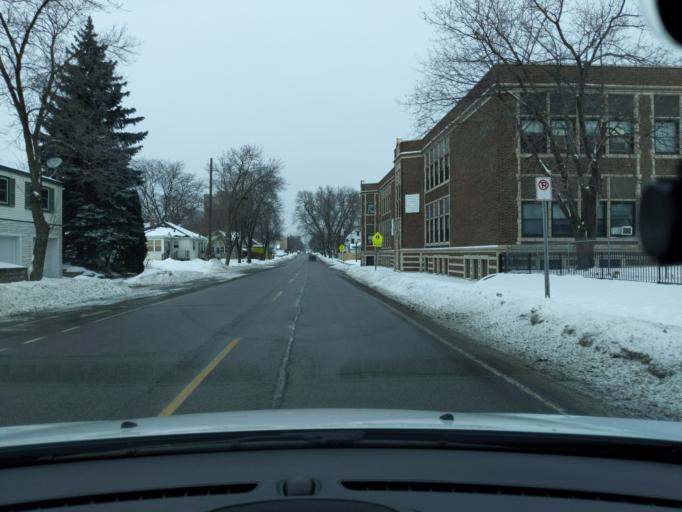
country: US
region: Minnesota
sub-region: Ramsey County
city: Falcon Heights
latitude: 44.9603
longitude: -93.1568
